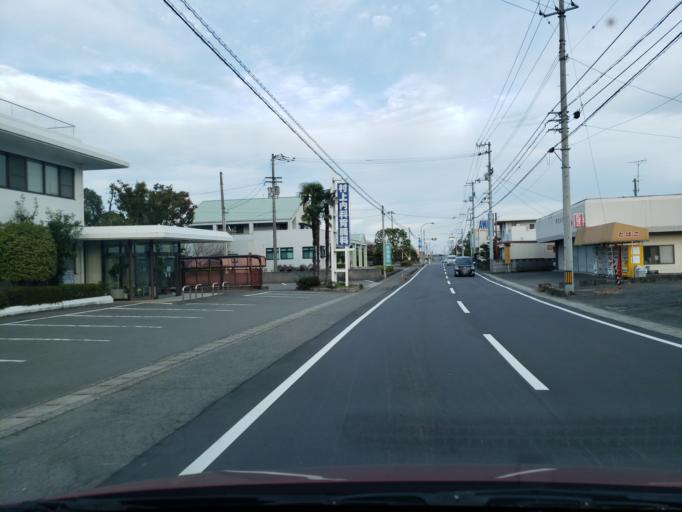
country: JP
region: Tokushima
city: Wakimachi
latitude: 34.0784
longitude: 134.2467
